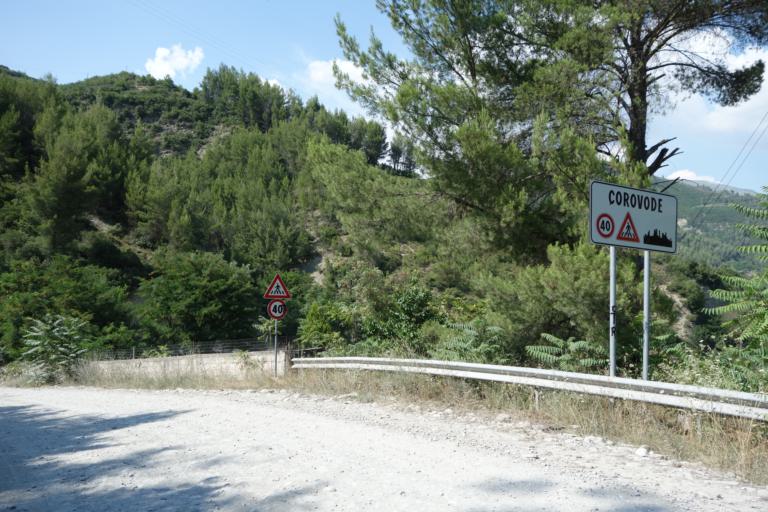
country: AL
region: Berat
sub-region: Rrethi i Skraparit
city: Corovode
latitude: 40.5059
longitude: 20.2244
